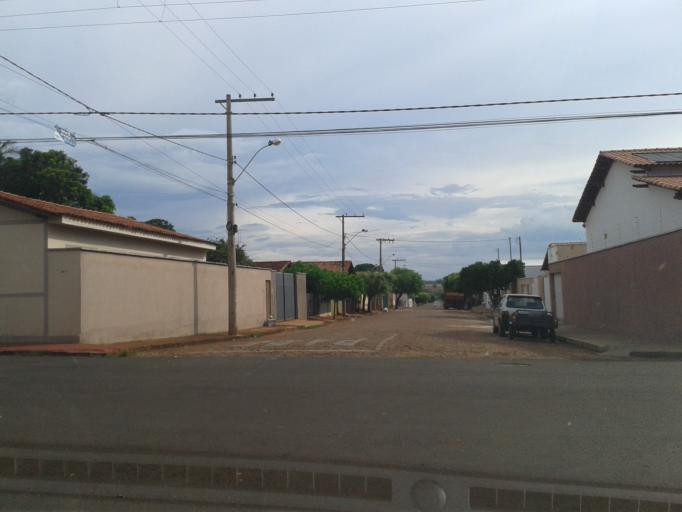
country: BR
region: Minas Gerais
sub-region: Centralina
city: Centralina
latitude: -18.7217
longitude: -49.2047
